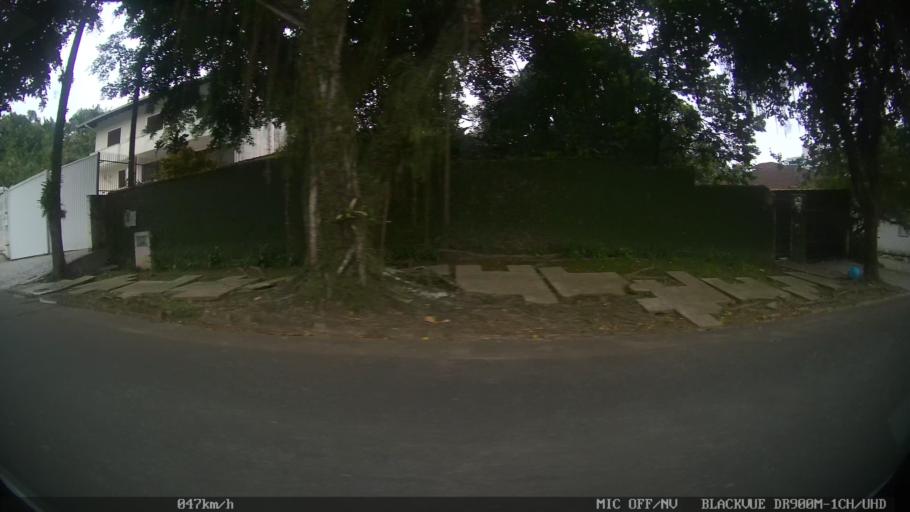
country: BR
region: Santa Catarina
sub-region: Joinville
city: Joinville
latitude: -26.2953
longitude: -48.8602
